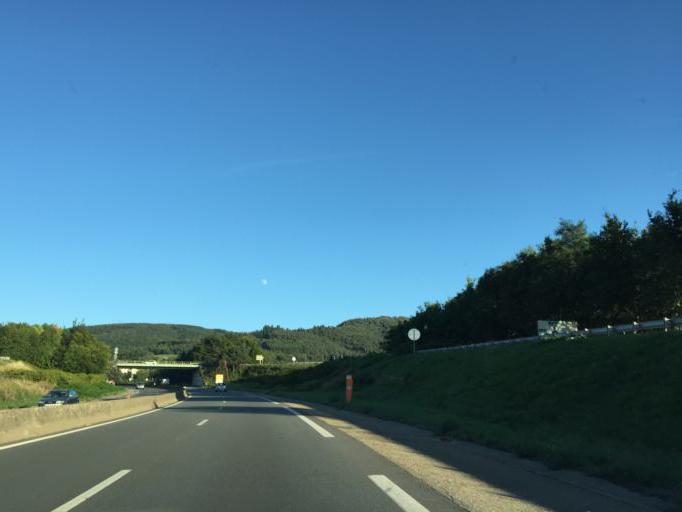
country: FR
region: Rhone-Alpes
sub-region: Departement de la Loire
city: Firminy
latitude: 45.3895
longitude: 4.2997
